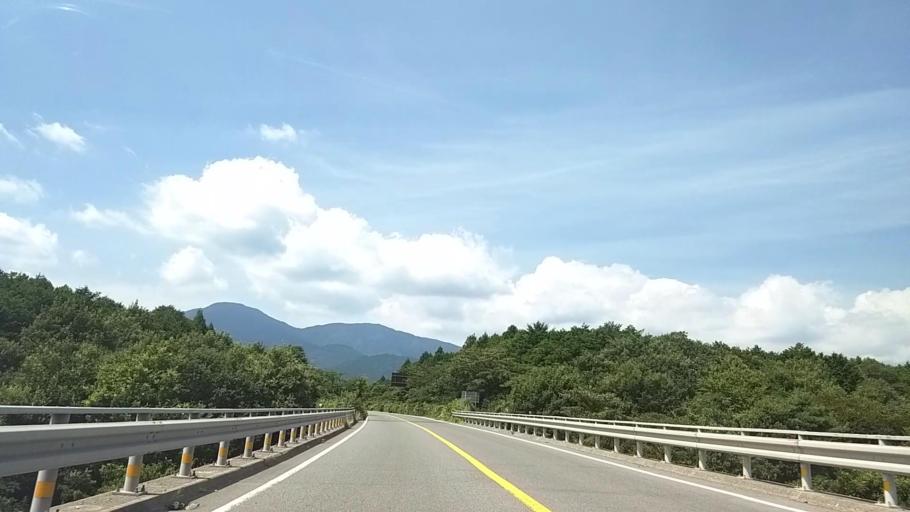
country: JP
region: Shizuoka
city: Fujinomiya
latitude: 35.3141
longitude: 138.5990
